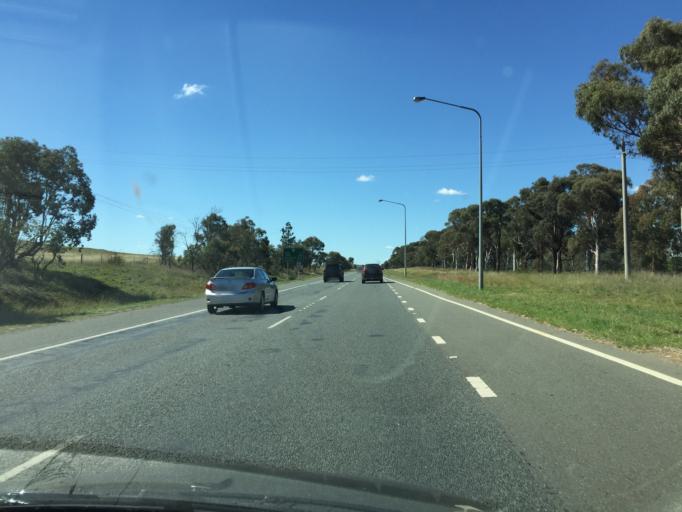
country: AU
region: Australian Capital Territory
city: Macarthur
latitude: -35.3799
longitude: 149.1698
